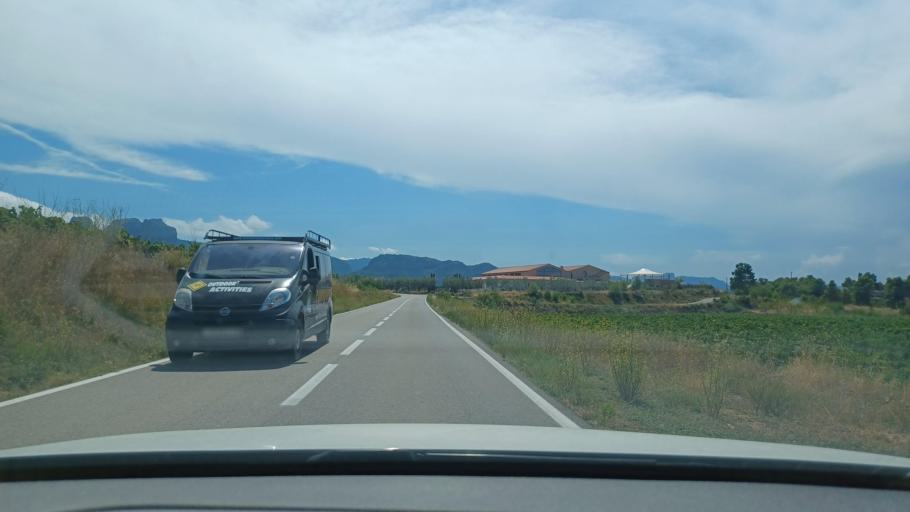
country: ES
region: Catalonia
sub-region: Provincia de Tarragona
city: Horta de Sant Joan
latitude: 40.9436
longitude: 0.3166
